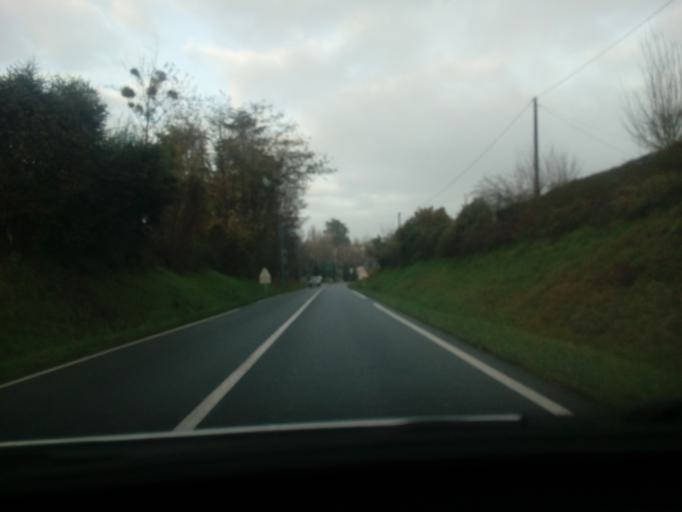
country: FR
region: Poitou-Charentes
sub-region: Departement de la Charente-Maritime
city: Jonzac
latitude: 45.4449
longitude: -0.4241
